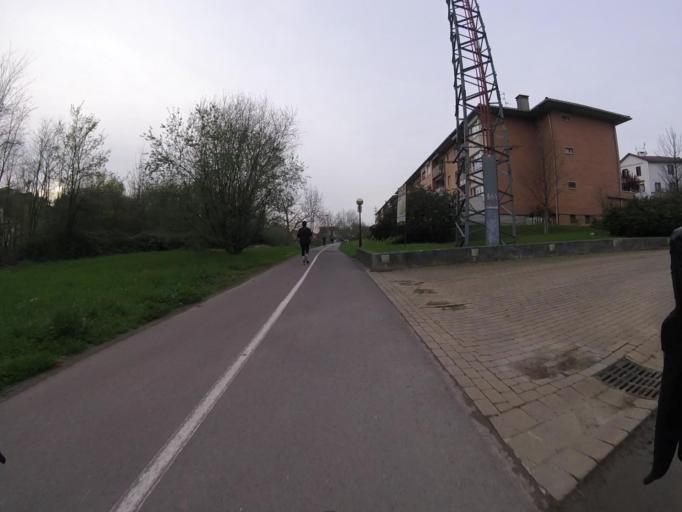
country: ES
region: Basque Country
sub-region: Provincia de Guipuzcoa
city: Errenteria
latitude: 43.2976
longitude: -1.8735
